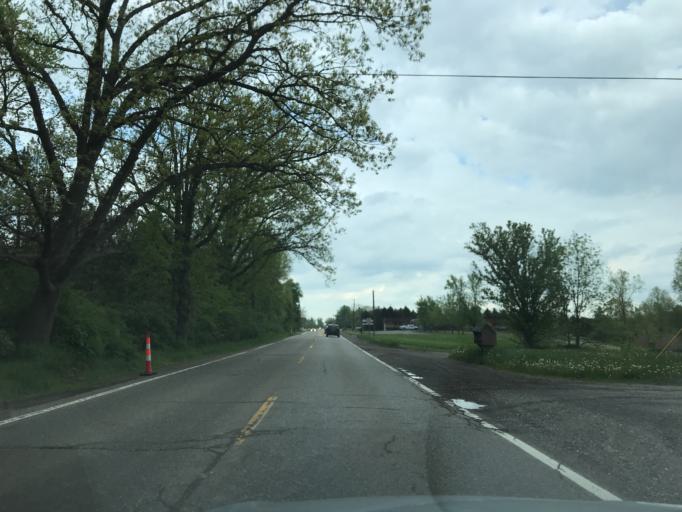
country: US
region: Michigan
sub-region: Oakland County
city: South Lyon
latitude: 42.4799
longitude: -83.6526
